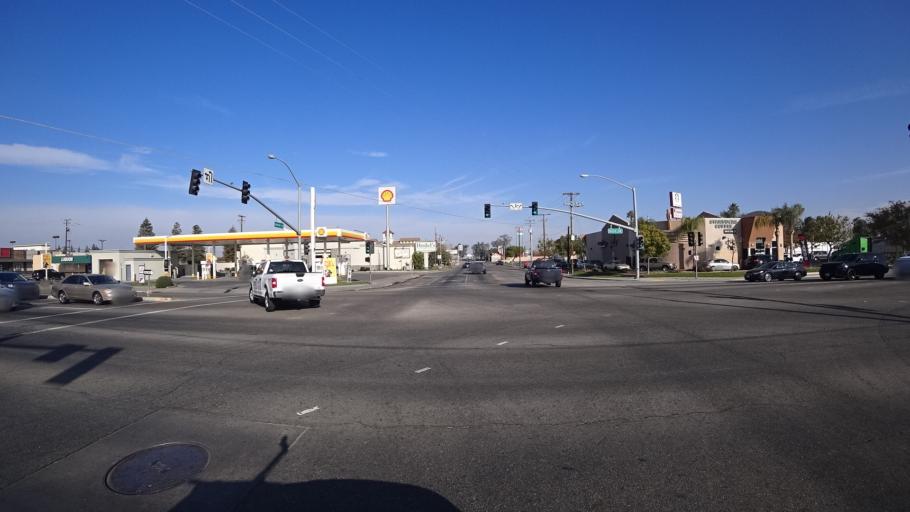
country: US
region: California
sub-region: Kern County
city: Oildale
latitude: 35.4122
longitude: -119.0588
